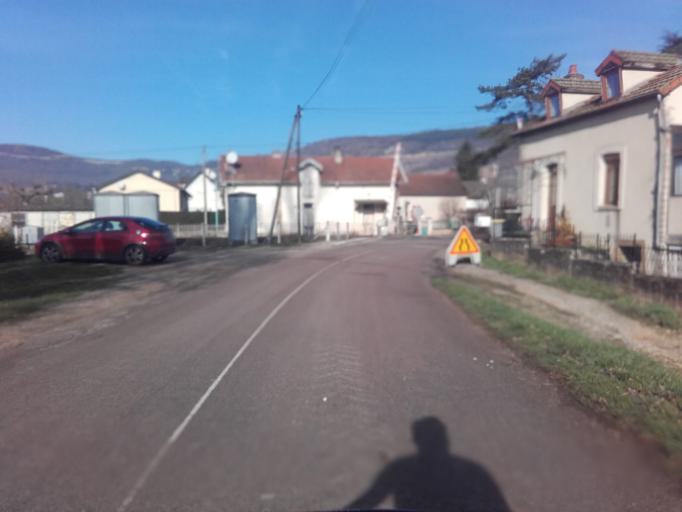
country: FR
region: Bourgogne
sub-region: Departement de Saone-et-Loire
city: Chagny
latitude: 46.9072
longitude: 4.6950
